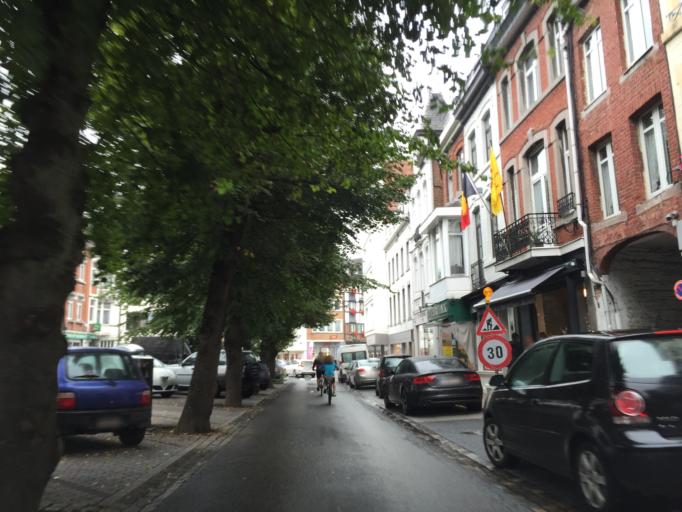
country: BE
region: Wallonia
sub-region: Province de Liege
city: Spa
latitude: 50.4912
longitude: 5.8630
